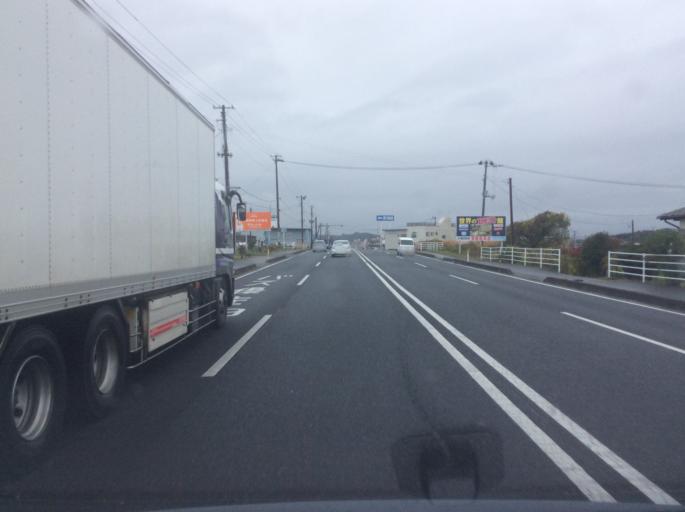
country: JP
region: Fukushima
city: Iwaki
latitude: 37.0765
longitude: 140.9569
